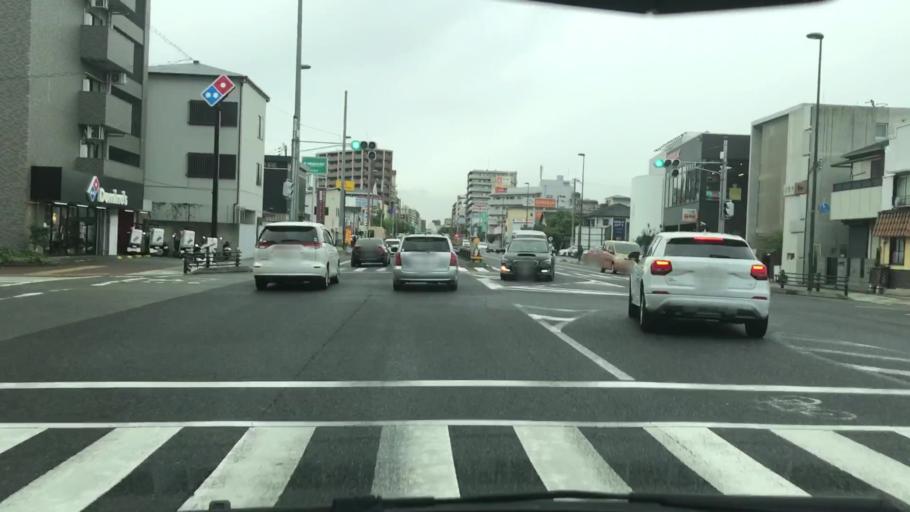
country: JP
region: Hyogo
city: Nishinomiya-hama
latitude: 34.7370
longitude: 135.3266
